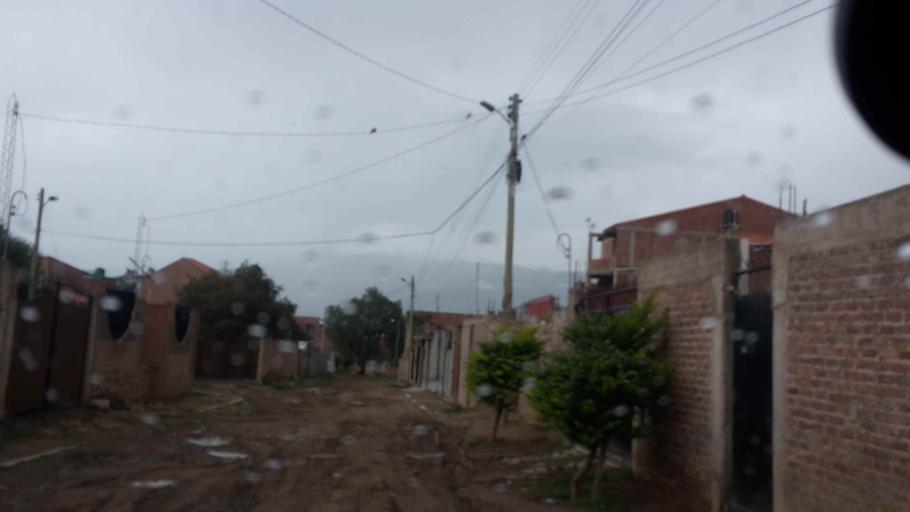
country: BO
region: Cochabamba
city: Cochabamba
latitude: -17.4481
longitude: -66.1569
